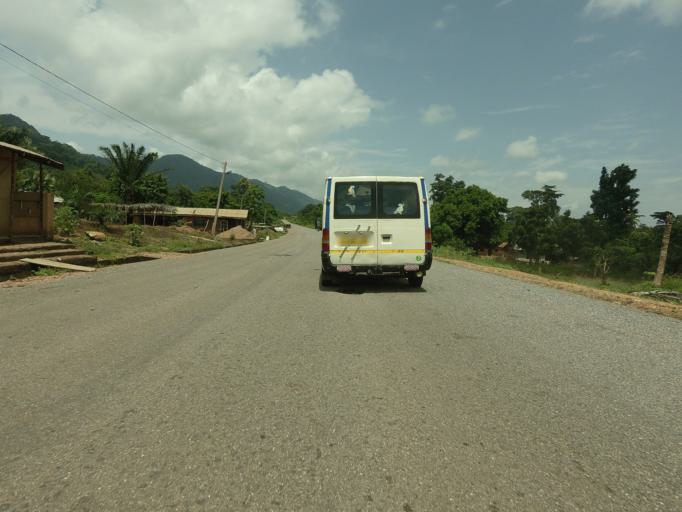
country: GH
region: Volta
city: Ho
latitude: 6.7848
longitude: 0.3661
